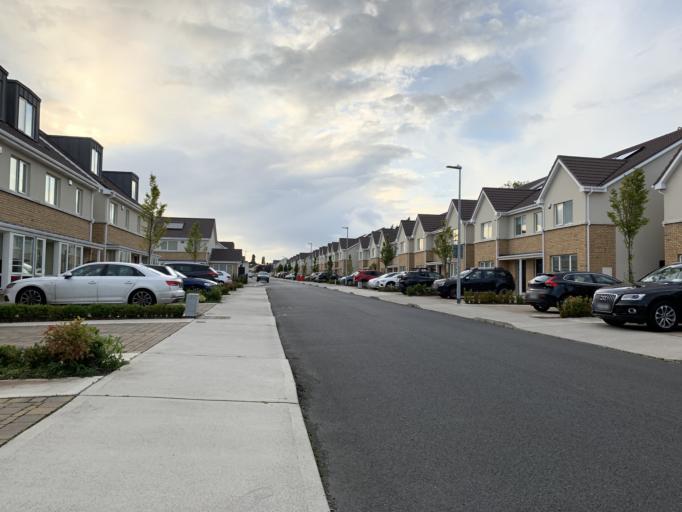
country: IE
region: Leinster
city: Castleknock
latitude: 53.3702
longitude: -6.3811
